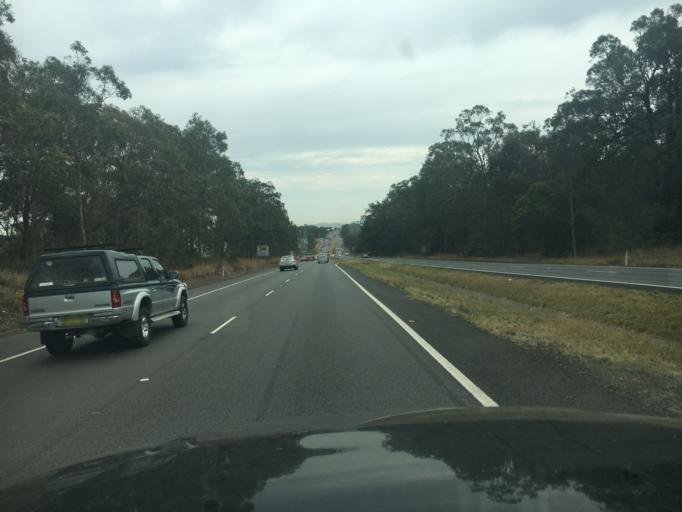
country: AU
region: New South Wales
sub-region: Maitland Municipality
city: East Maitland
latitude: -32.7666
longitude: 151.6006
